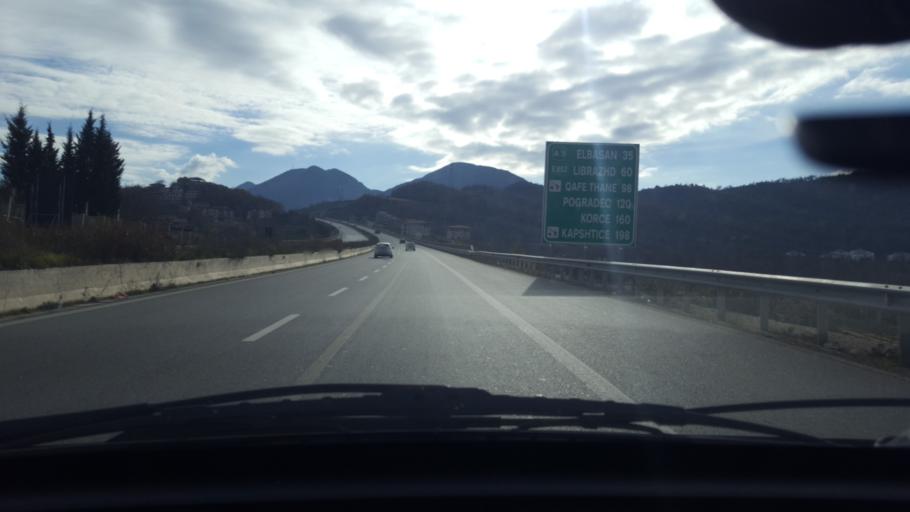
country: AL
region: Tirane
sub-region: Rrethi i Tiranes
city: Petrele
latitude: 41.2778
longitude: 19.8559
